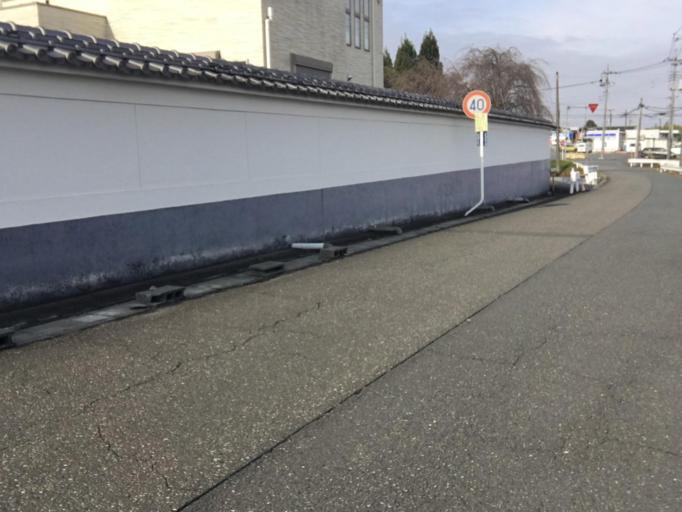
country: JP
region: Saitama
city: Yorii
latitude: 36.1414
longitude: 139.1996
